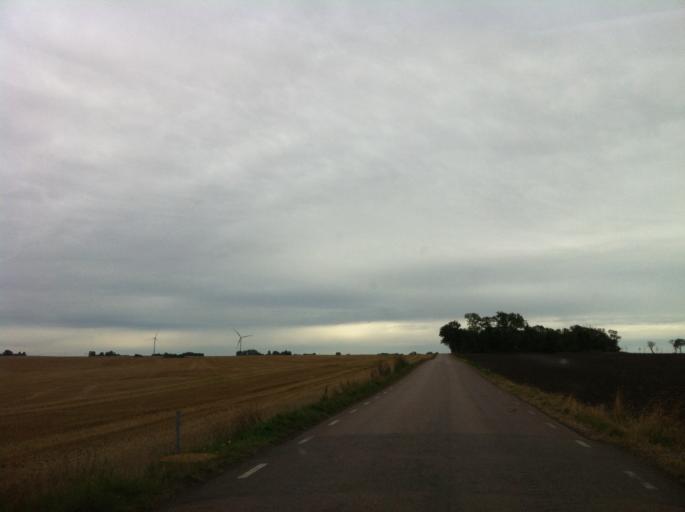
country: SE
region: Skane
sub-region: Landskrona
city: Asmundtorp
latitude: 55.9139
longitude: 13.0027
